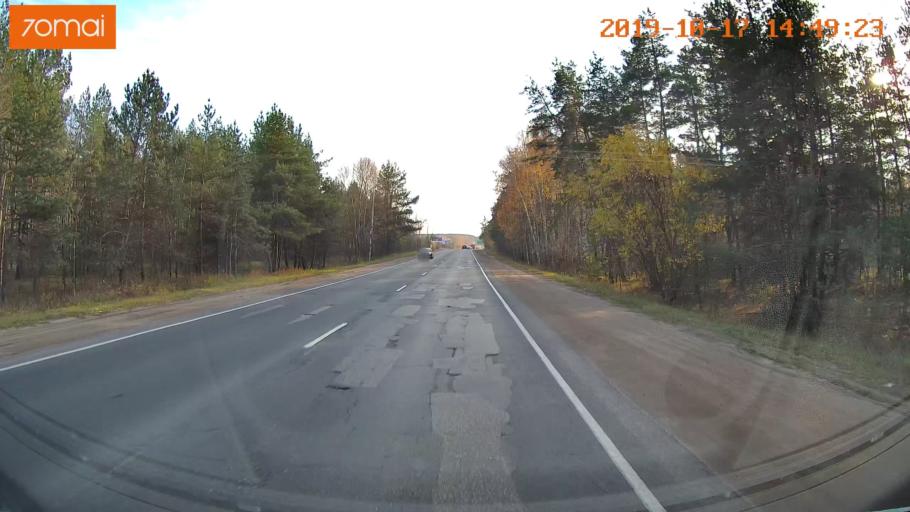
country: RU
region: Rjazan
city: Polyany
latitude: 54.7477
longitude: 39.8398
